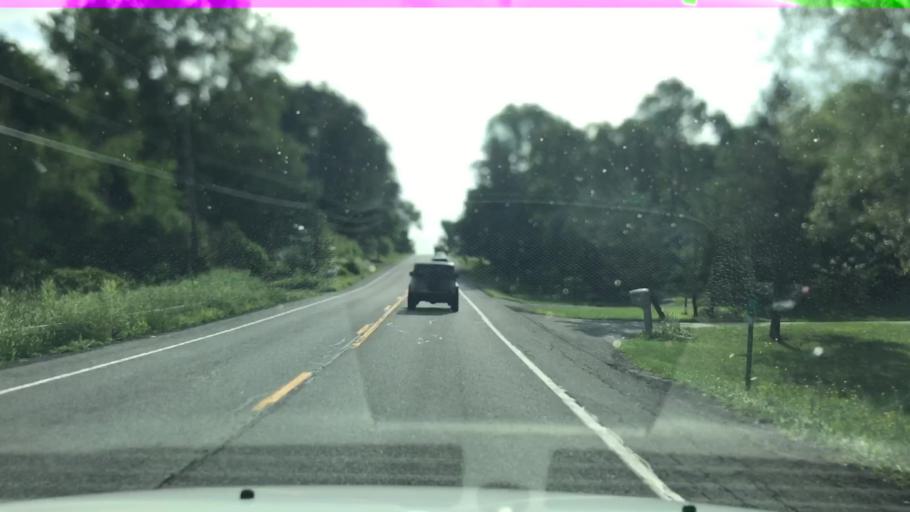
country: US
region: New York
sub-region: Erie County
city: Town Line
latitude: 42.8561
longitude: -78.5891
